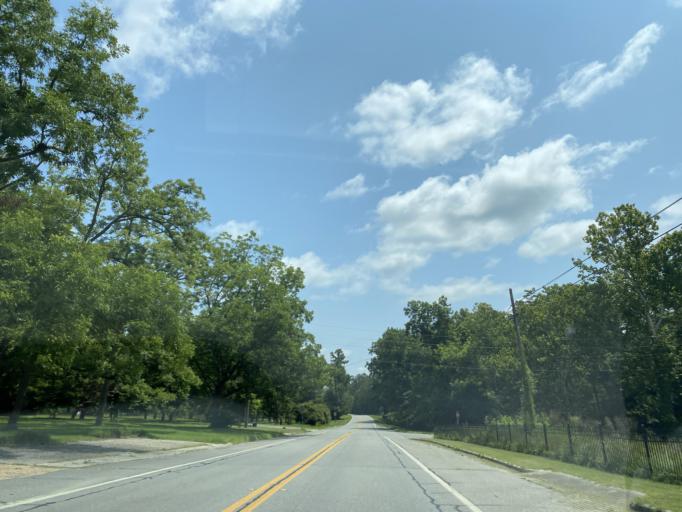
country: US
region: Georgia
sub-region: Wilcox County
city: Abbeville
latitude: 31.9904
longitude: -83.1980
